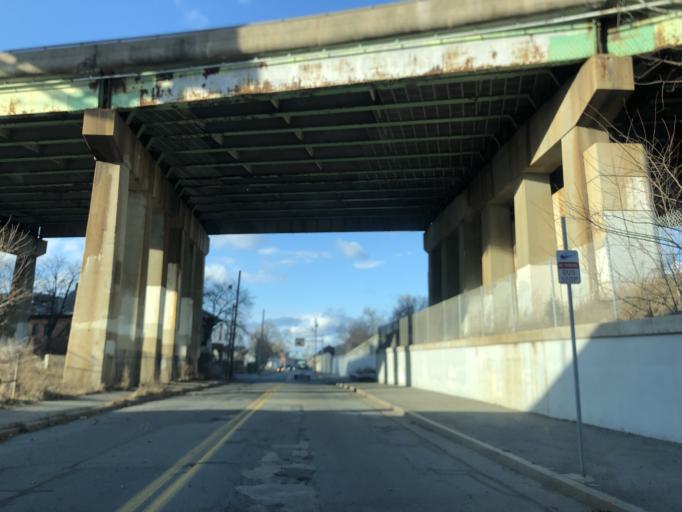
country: US
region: Massachusetts
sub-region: Bristol County
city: New Bedford
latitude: 41.6536
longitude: -70.9302
